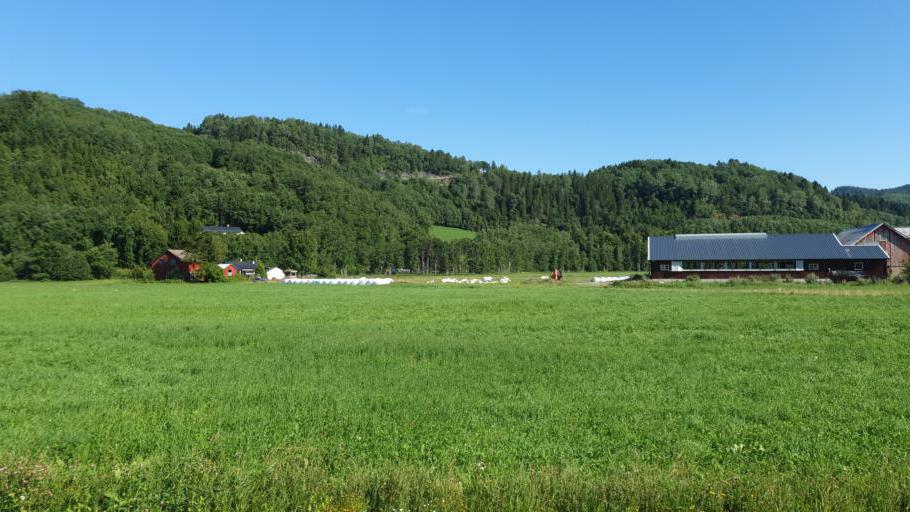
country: NO
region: Sor-Trondelag
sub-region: Orkdal
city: Orkanger
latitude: 63.2078
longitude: 9.7861
